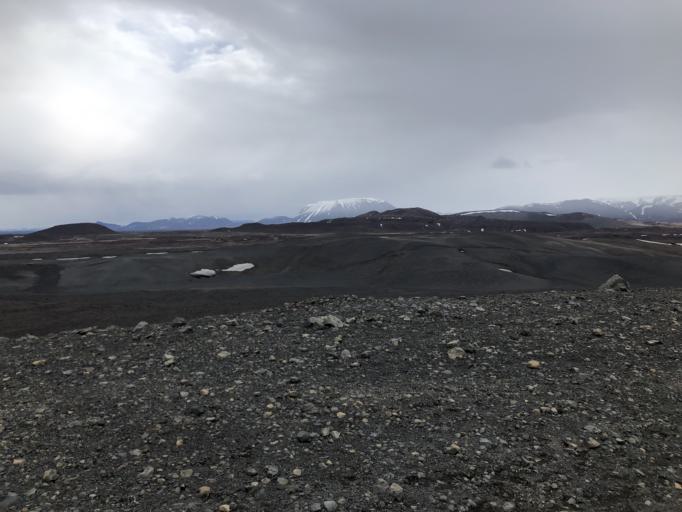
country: IS
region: Northeast
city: Laugar
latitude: 65.6052
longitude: -16.8629
